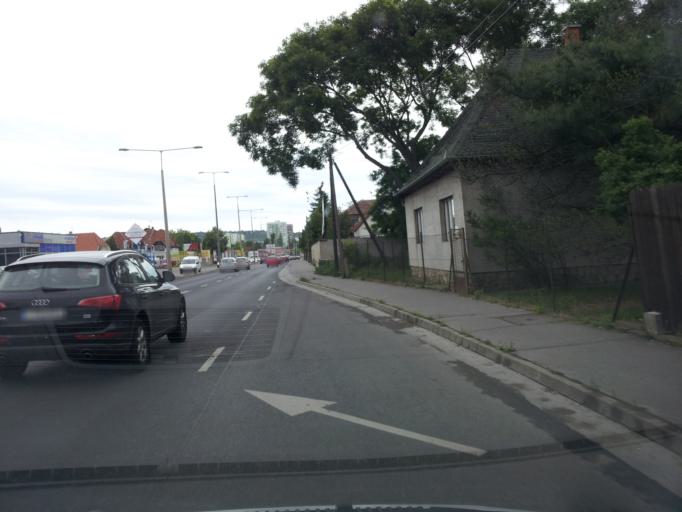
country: HU
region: Pest
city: Budakalasz
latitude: 47.5873
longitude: 19.0501
